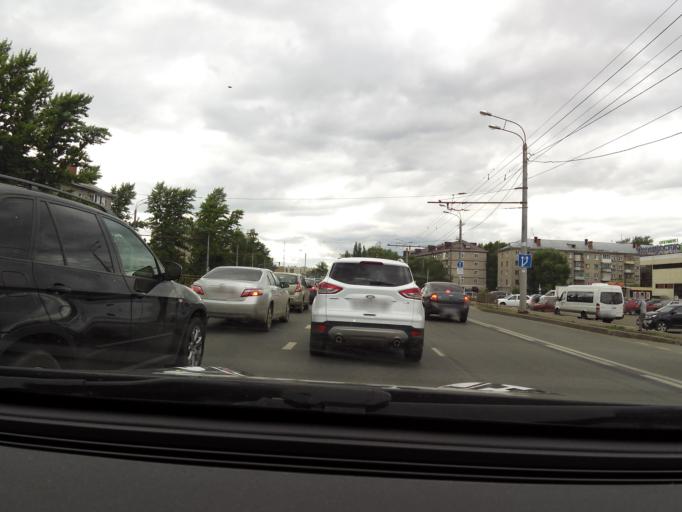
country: RU
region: Tatarstan
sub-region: Gorod Kazan'
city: Kazan
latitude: 55.8169
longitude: 49.0646
